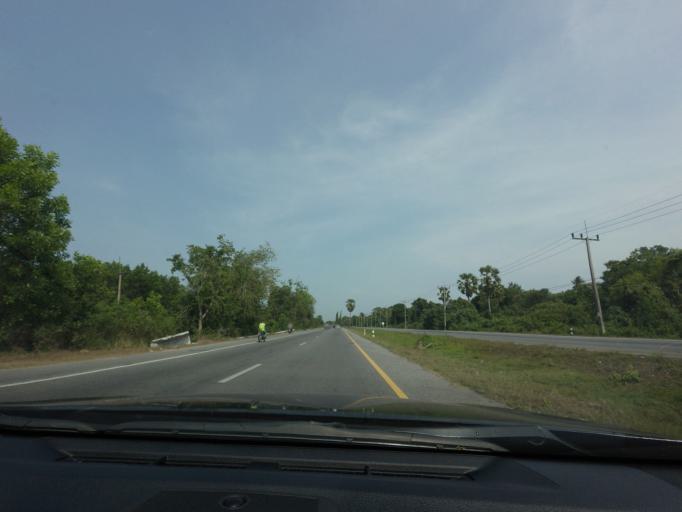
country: TH
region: Pattani
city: Yaring
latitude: 6.8249
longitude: 101.3965
